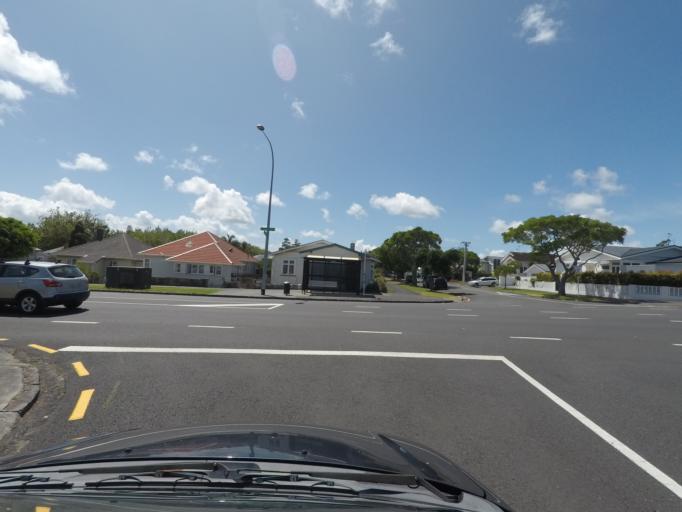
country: NZ
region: Auckland
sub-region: Auckland
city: Auckland
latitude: -36.8570
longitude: 174.7214
